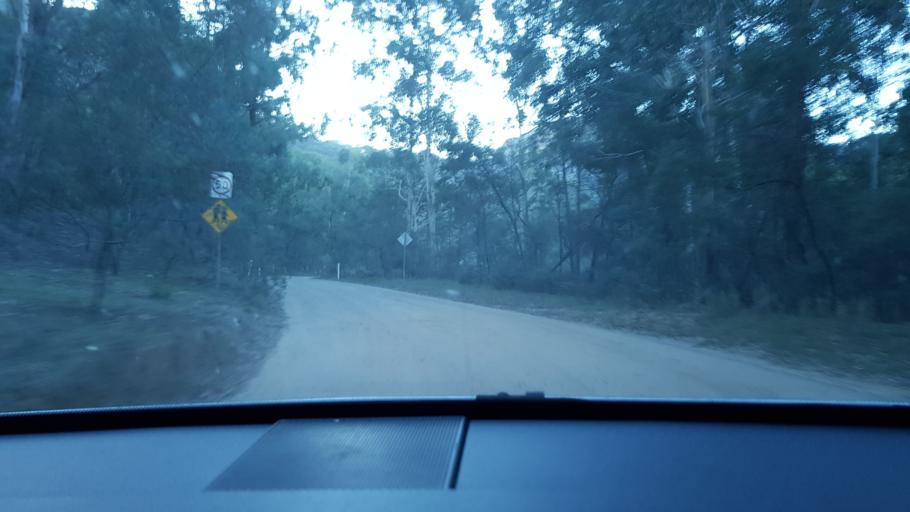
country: AU
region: New South Wales
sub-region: Lithgow
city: Portland
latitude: -33.1821
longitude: 150.2373
